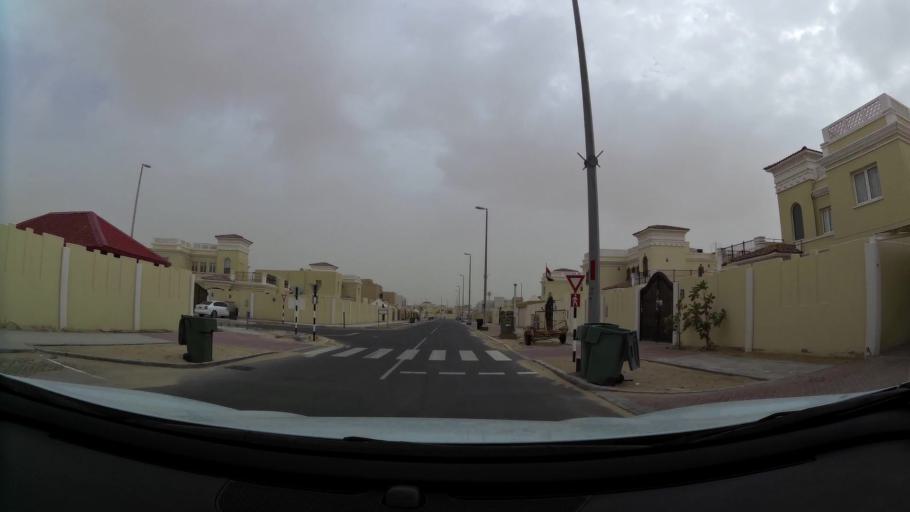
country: AE
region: Abu Dhabi
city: Abu Dhabi
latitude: 24.4532
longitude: 54.7374
